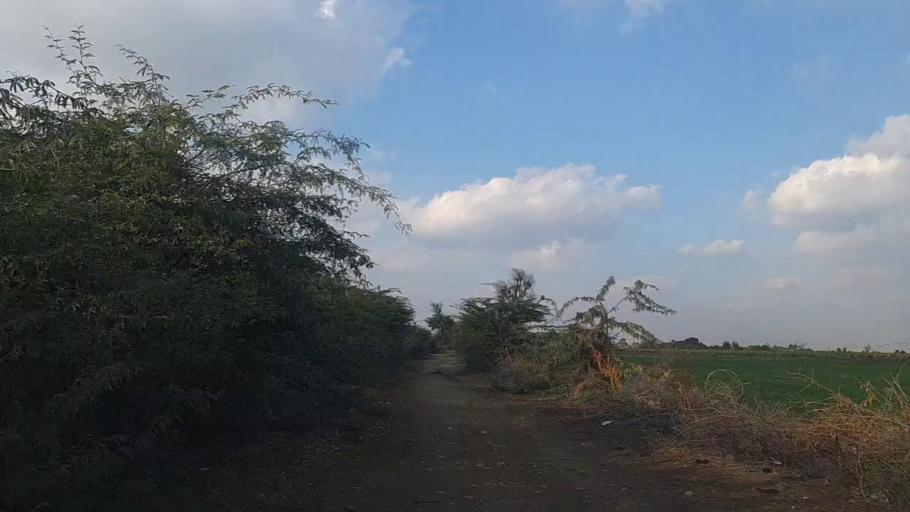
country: PK
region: Sindh
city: Tando Mittha Khan
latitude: 25.9362
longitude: 69.2509
